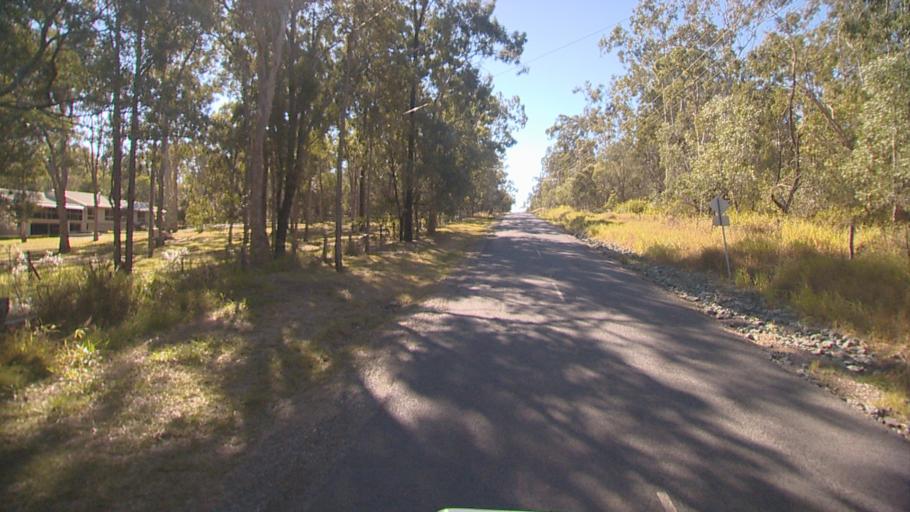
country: AU
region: Queensland
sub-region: Logan
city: Chambers Flat
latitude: -27.8135
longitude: 153.0713
